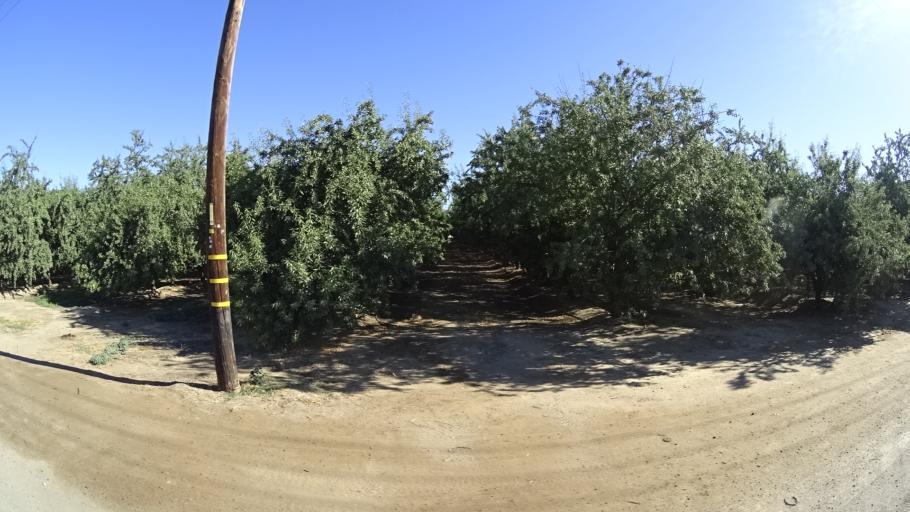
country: US
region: California
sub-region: Fresno County
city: Easton
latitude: 36.6923
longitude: -119.8066
